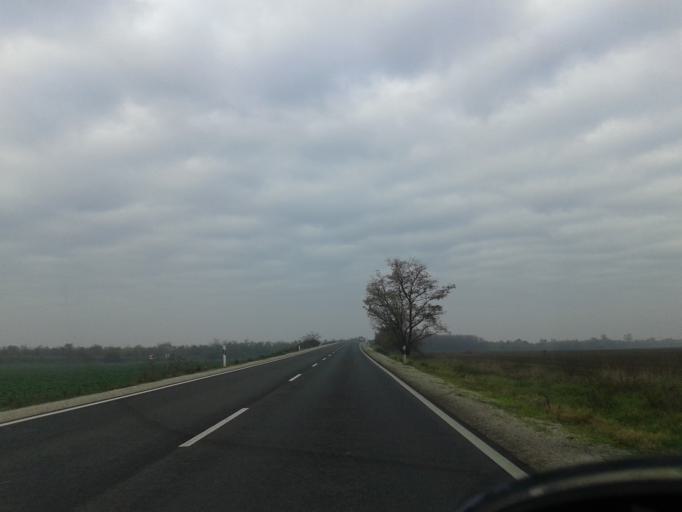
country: HU
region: Fejer
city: Ercsi
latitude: 47.2729
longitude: 18.8804
